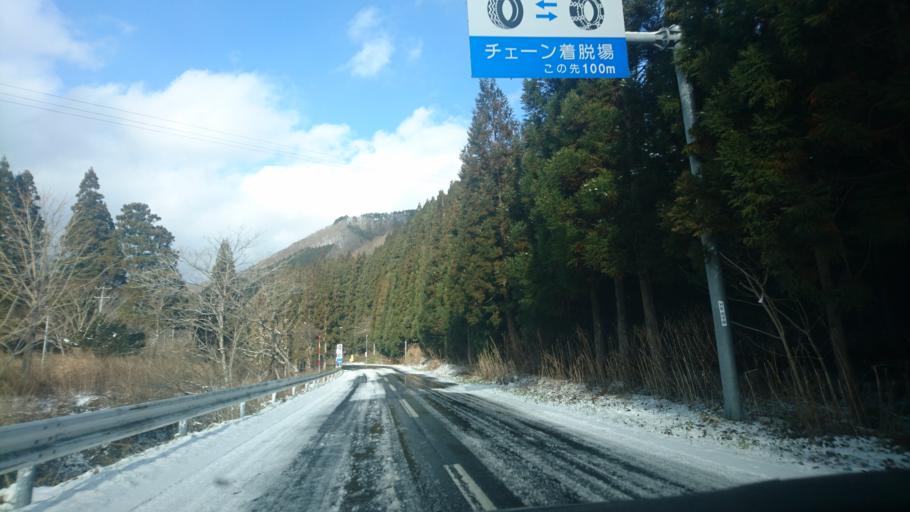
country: JP
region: Iwate
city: Tono
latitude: 39.1636
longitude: 141.3659
